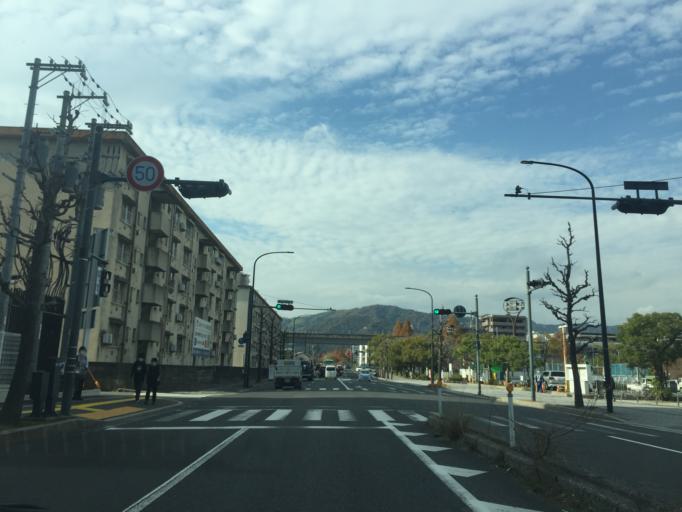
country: JP
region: Hiroshima
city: Hiroshima-shi
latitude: 34.4160
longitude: 132.4668
